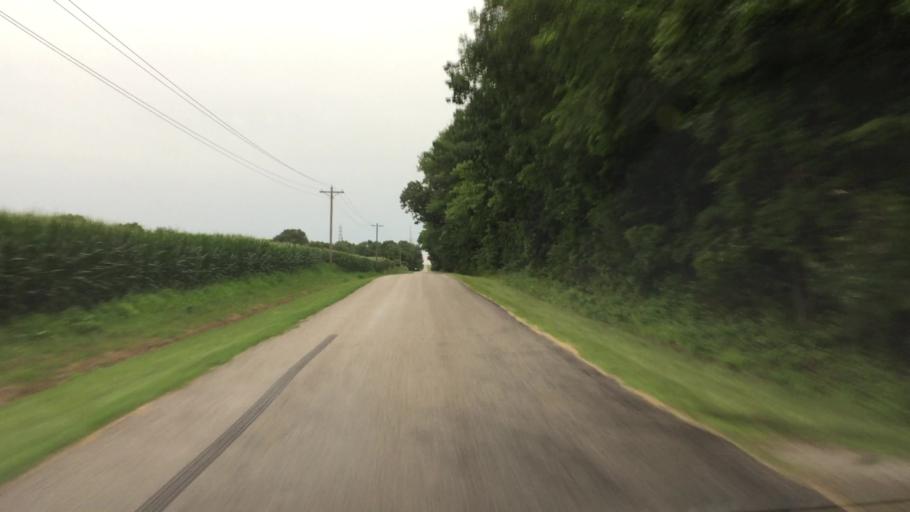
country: US
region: Illinois
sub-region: Hancock County
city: Hamilton
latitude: 40.4263
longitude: -91.3609
